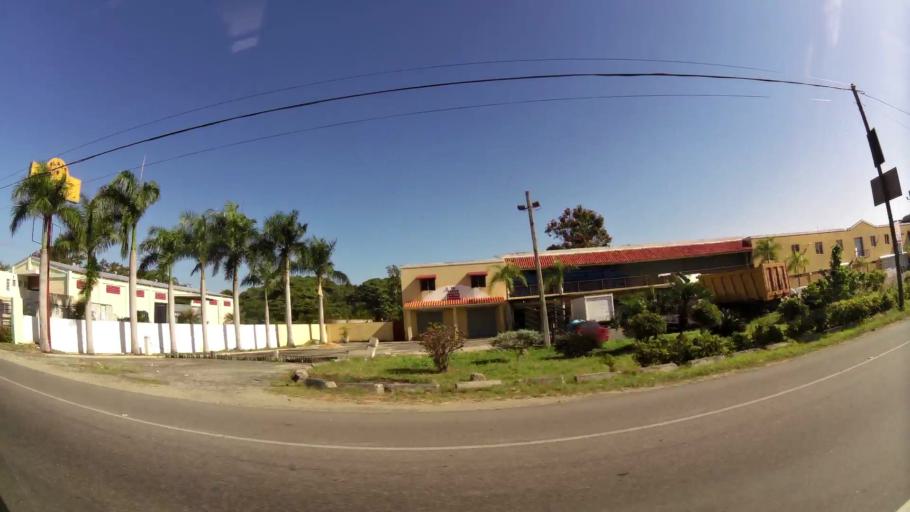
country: DO
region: San Cristobal
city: San Cristobal
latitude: 18.4322
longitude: -70.0666
